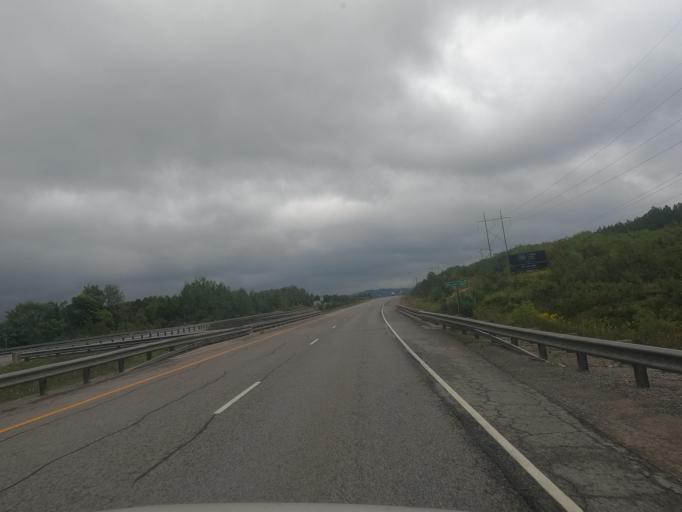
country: CA
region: Ontario
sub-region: Algoma
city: Sault Ste. Marie
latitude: 46.5576
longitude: -84.2165
